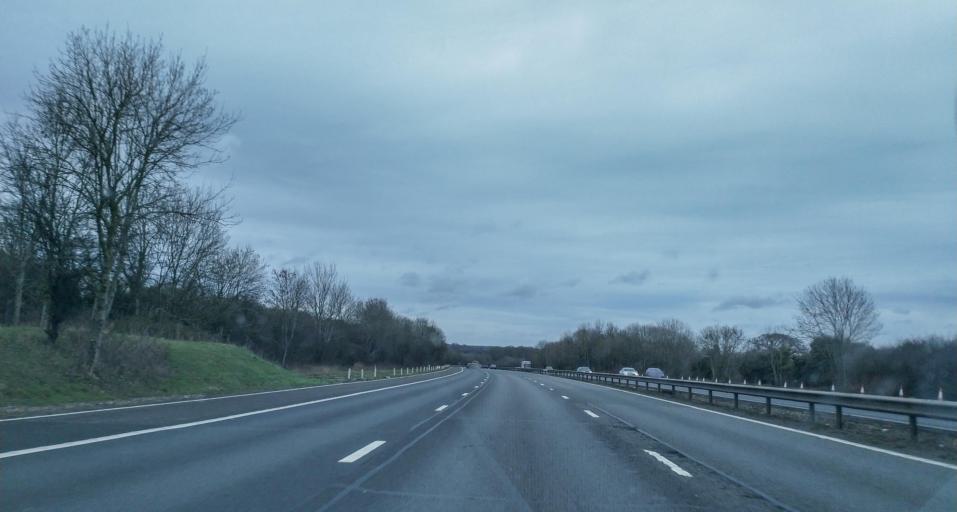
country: GB
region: England
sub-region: Buckinghamshire
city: High Wycombe
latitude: 51.6105
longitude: -0.7269
